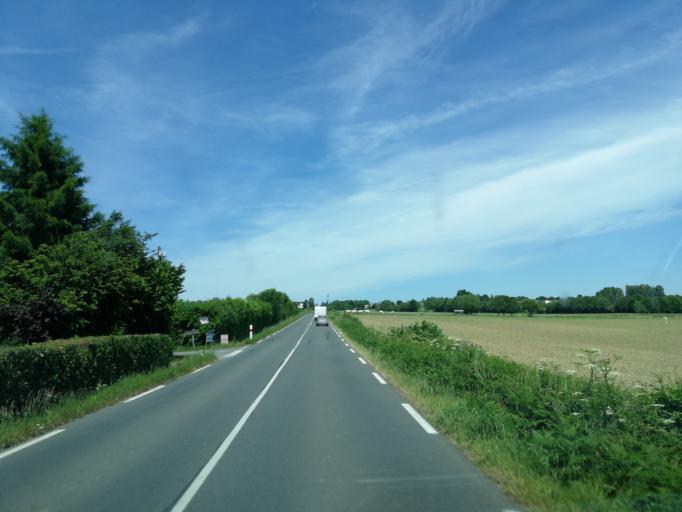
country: FR
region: Pays de la Loire
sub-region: Departement de la Vendee
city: La Tardiere
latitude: 46.6663
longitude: -0.7260
